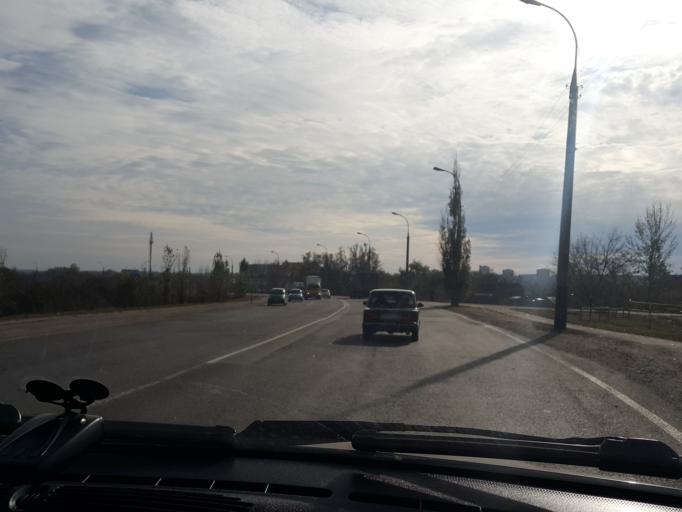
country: RU
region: Tambov
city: Tambov
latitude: 52.7266
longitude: 41.4651
